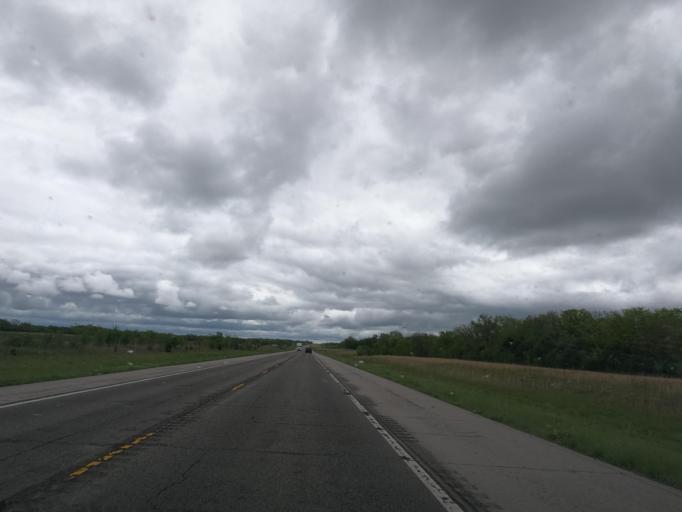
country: US
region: Kansas
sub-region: Montgomery County
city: Cherryvale
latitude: 37.3435
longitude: -95.4433
